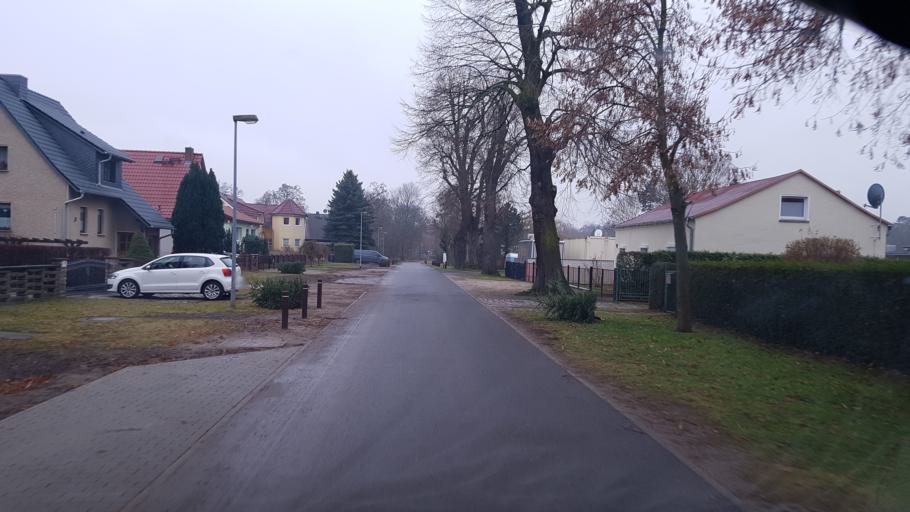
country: DE
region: Brandenburg
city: Stahnsdorf
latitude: 52.3623
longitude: 13.1959
